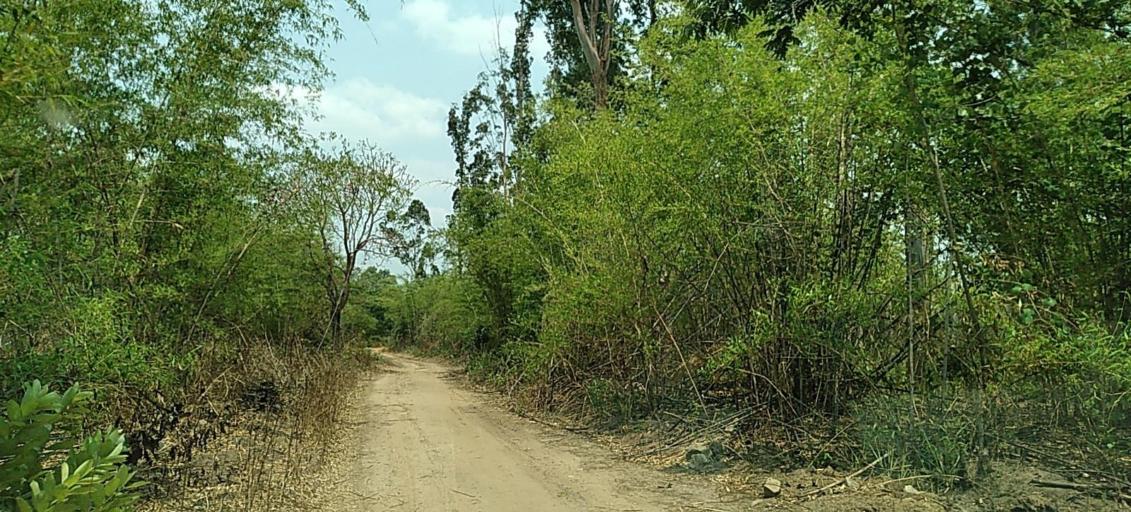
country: ZM
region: Copperbelt
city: Kalulushi
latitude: -12.7581
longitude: 28.0267
